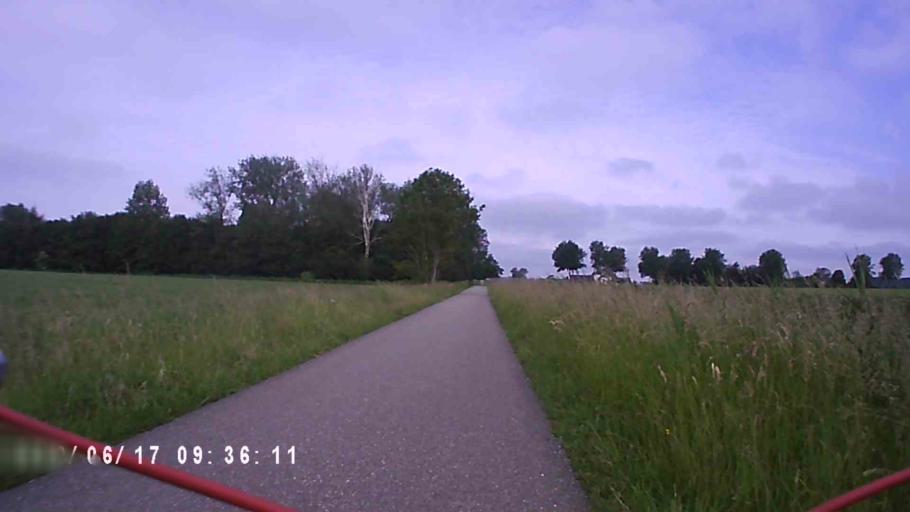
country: NL
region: Groningen
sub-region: Gemeente De Marne
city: Ulrum
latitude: 53.3505
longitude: 6.3728
